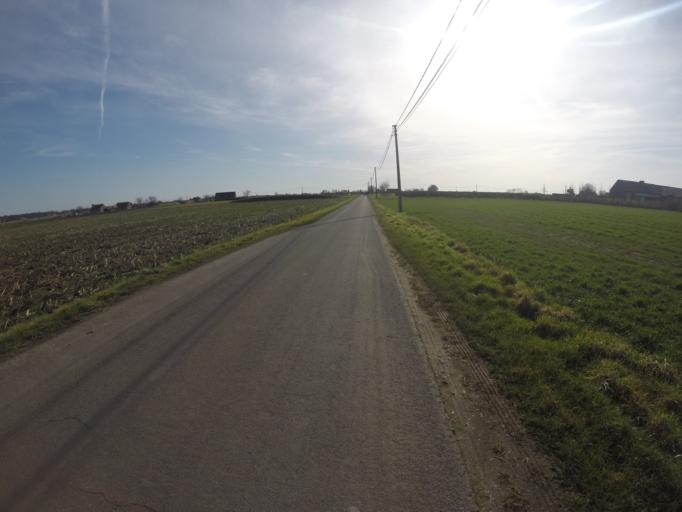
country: BE
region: Flanders
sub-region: Provincie West-Vlaanderen
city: Wingene
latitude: 51.0886
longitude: 3.2662
